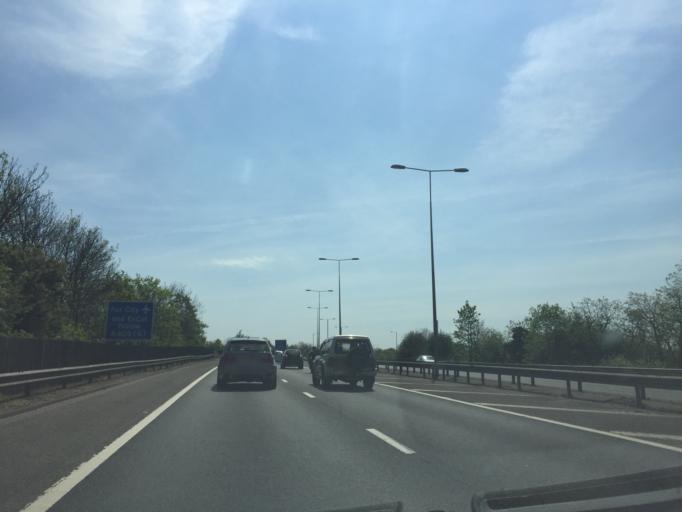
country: GB
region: England
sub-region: Essex
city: Buckhurst Hill
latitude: 51.6062
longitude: 0.0488
